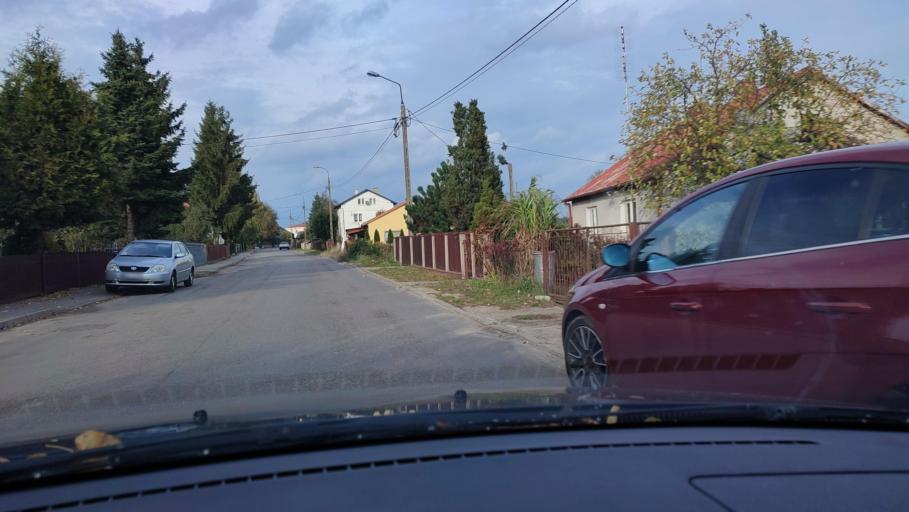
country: PL
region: Masovian Voivodeship
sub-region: Powiat mlawski
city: Mlawa
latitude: 53.1355
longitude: 20.3646
